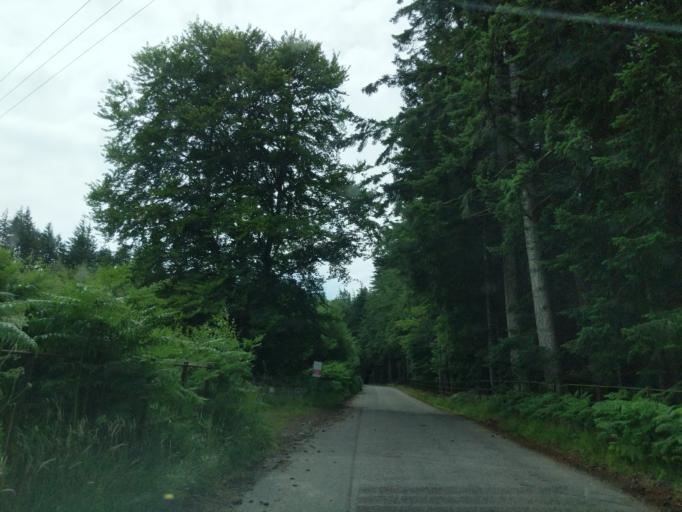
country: GB
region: Scotland
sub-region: Aberdeenshire
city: Aboyne
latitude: 57.0670
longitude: -2.7795
